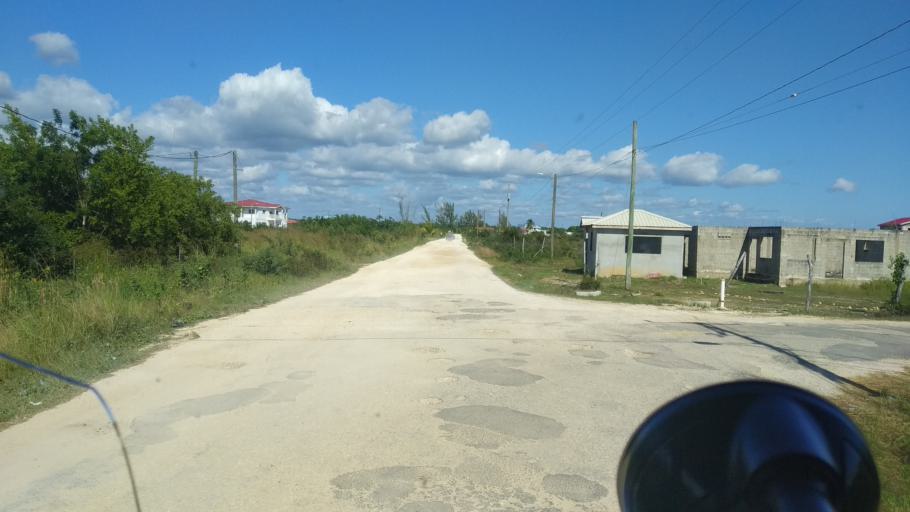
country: BZ
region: Belize
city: Belize City
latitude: 17.5606
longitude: -88.3035
